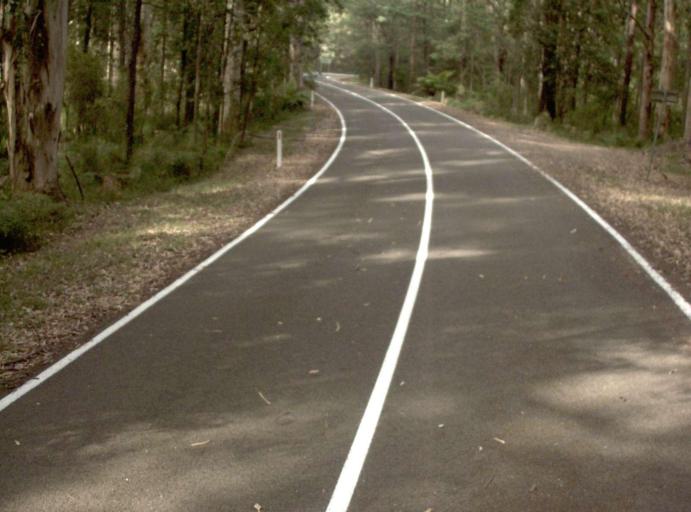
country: AU
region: Victoria
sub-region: Yarra Ranges
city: Badger Creek
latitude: -37.7003
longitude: 145.5727
